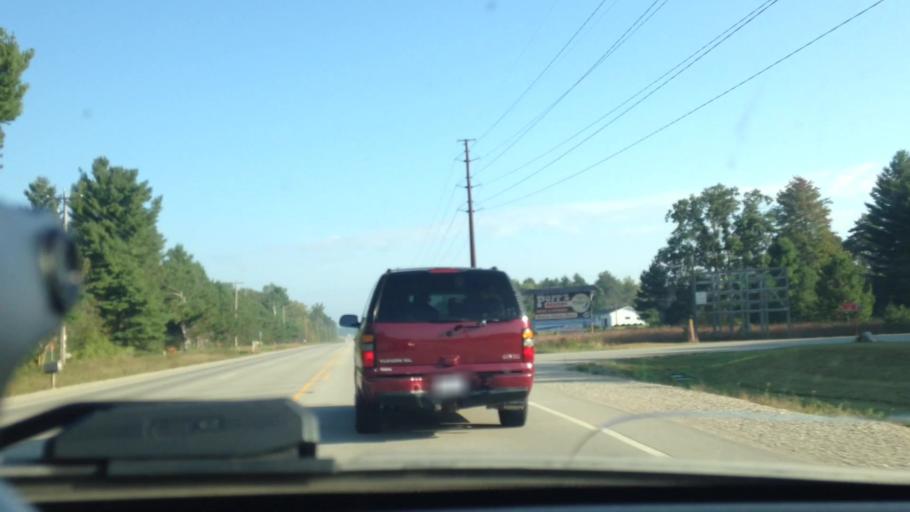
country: US
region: Wisconsin
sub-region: Marinette County
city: Peshtigo
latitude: 45.1871
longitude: -87.9953
